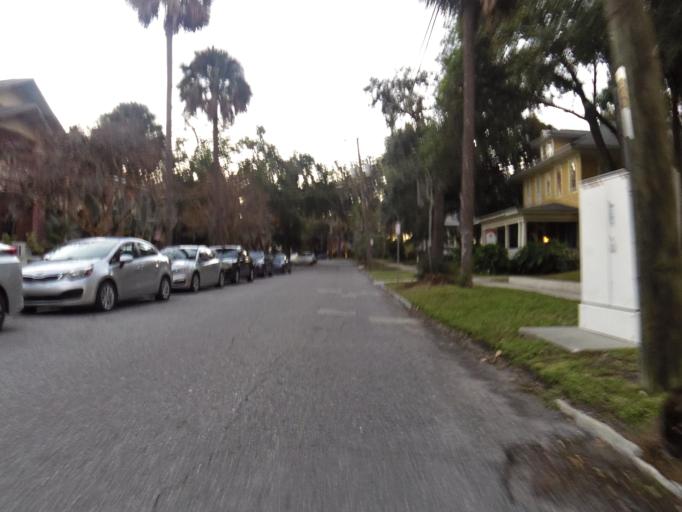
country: US
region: Florida
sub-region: Duval County
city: Jacksonville
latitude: 30.3118
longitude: -81.6776
